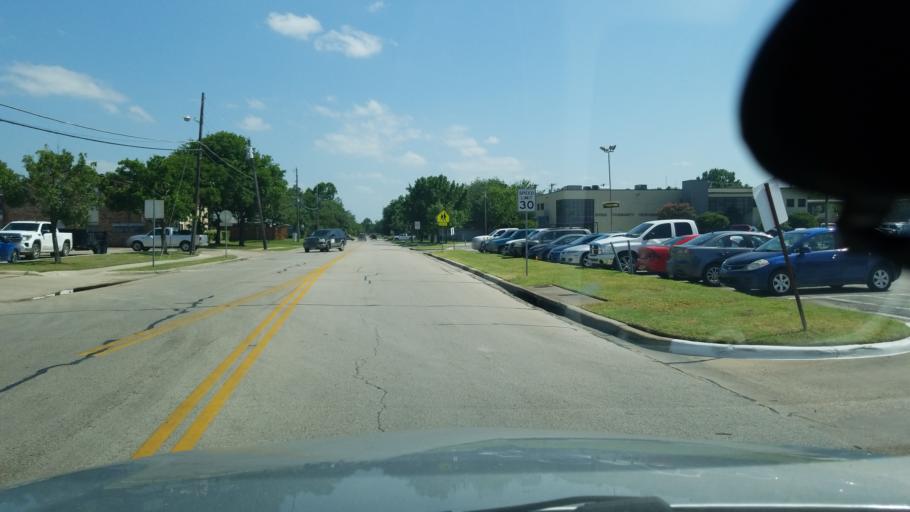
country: US
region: Texas
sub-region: Dallas County
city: Irving
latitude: 32.8145
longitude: -96.9635
